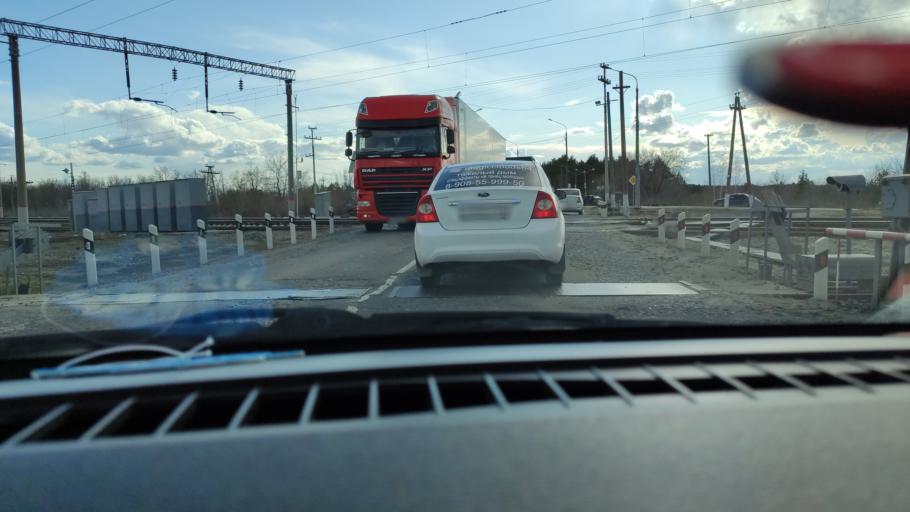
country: RU
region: Saratov
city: Sennoy
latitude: 52.1505
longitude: 46.9485
